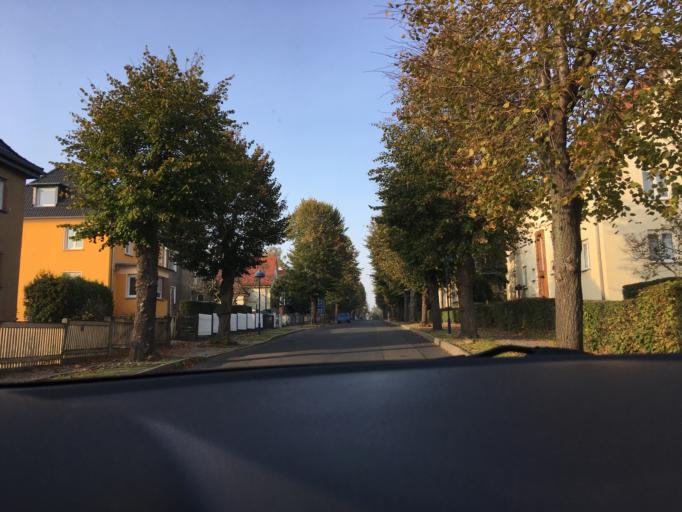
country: DE
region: Saxony
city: Rotha
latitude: 51.1972
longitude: 12.4174
